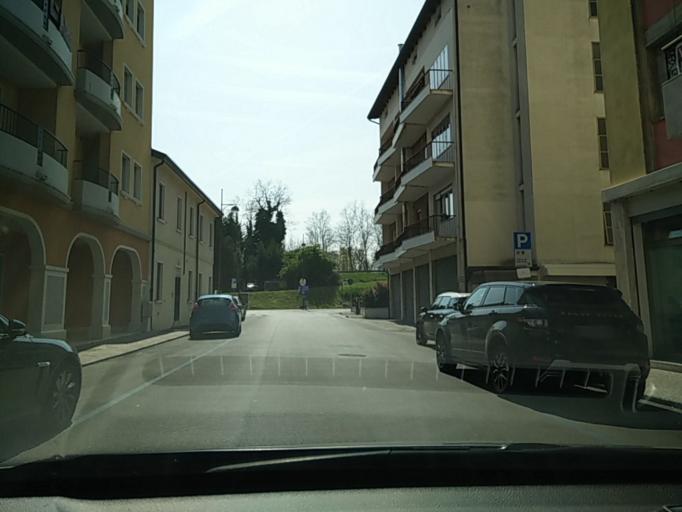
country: IT
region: Veneto
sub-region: Provincia di Venezia
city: San Dona di Piave
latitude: 45.6289
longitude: 12.5619
